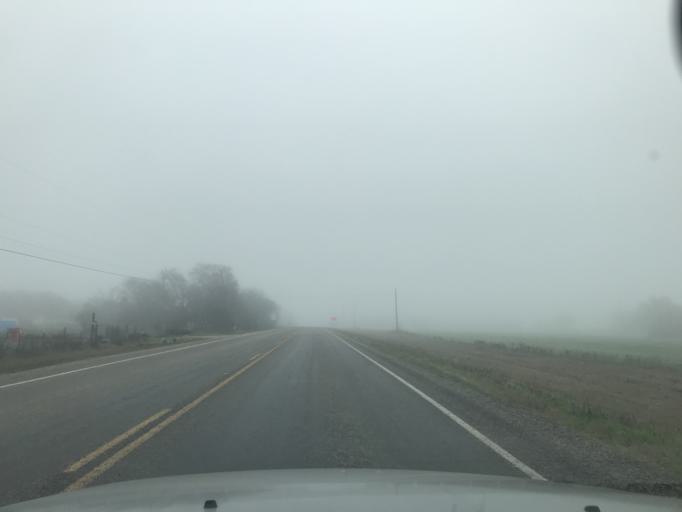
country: US
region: Texas
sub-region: Rockwall County
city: Royse City
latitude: 33.0052
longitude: -96.2963
